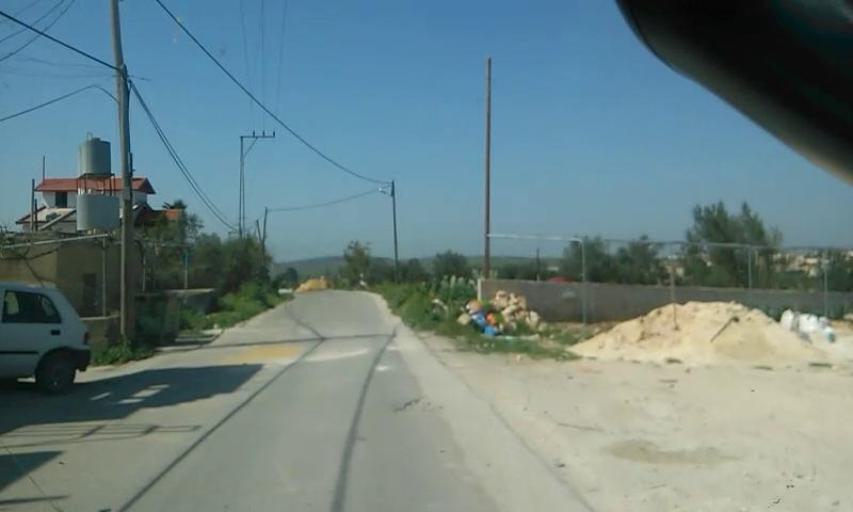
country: PS
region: West Bank
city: Al Majd
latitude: 31.4836
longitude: 34.9461
